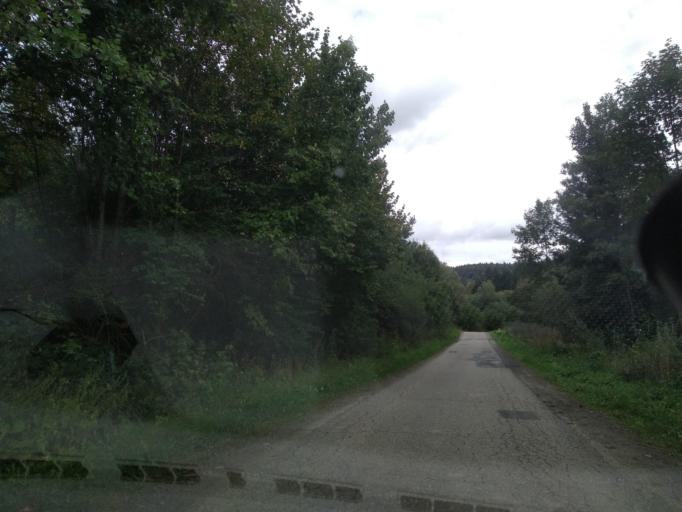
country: PL
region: Lesser Poland Voivodeship
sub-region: Powiat gorlicki
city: Uscie Gorlickie
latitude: 49.5223
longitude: 21.1598
